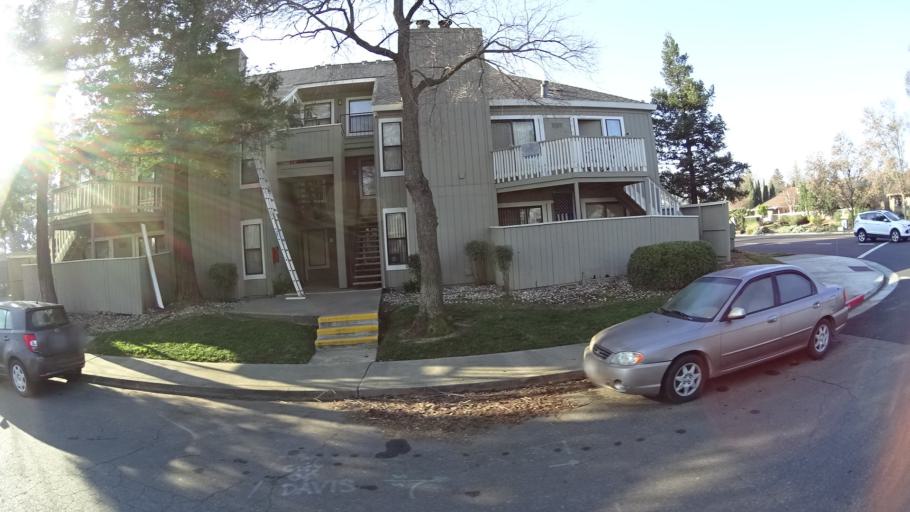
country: US
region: California
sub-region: Yolo County
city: Davis
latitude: 38.5564
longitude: -121.7868
